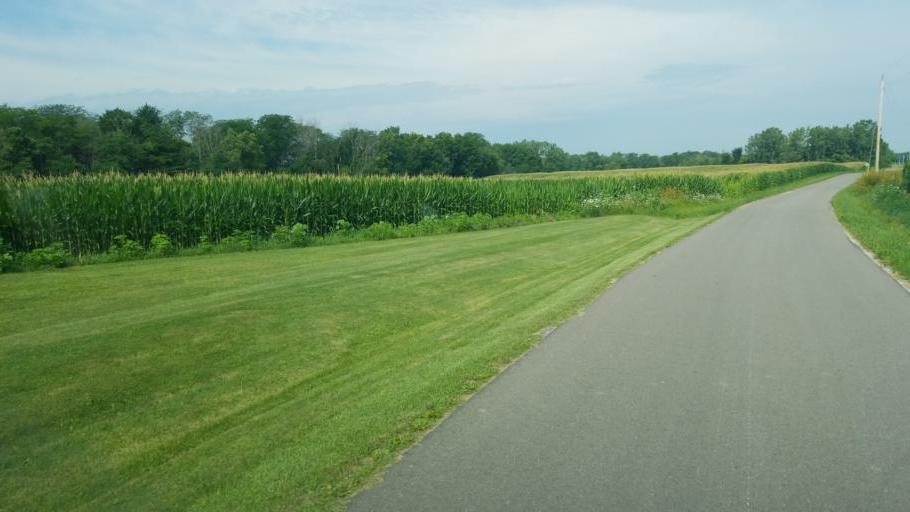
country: US
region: Ohio
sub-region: Wyandot County
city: Upper Sandusky
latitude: 40.6693
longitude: -83.3328
